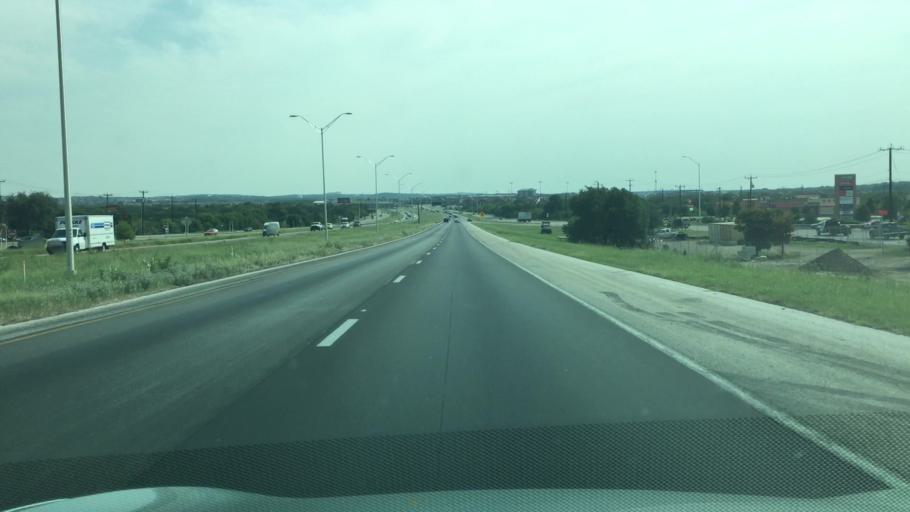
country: US
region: Texas
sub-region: Bexar County
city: Helotes
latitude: 29.5556
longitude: -98.6647
